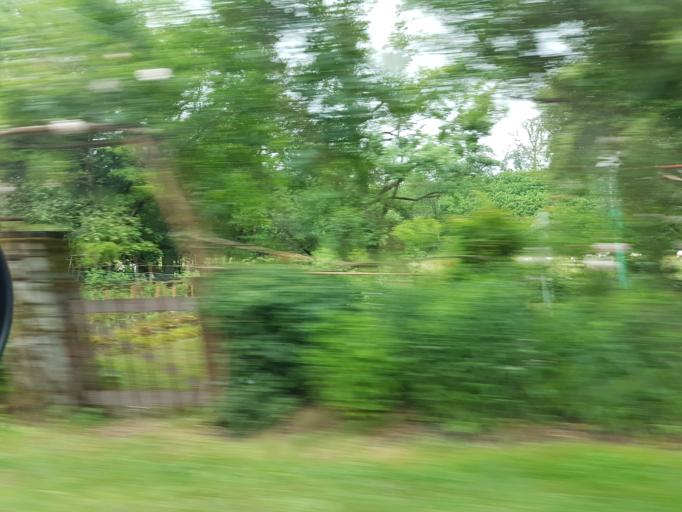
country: FR
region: Bourgogne
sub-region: Departement de la Nievre
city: Lormes
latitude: 47.1725
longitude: 3.8359
